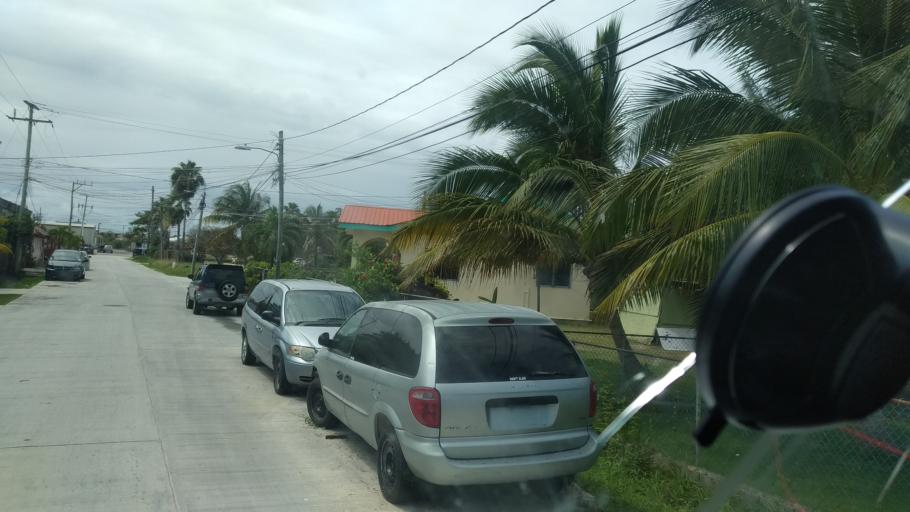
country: BZ
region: Belize
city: Belize City
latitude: 17.5130
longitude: -88.2019
